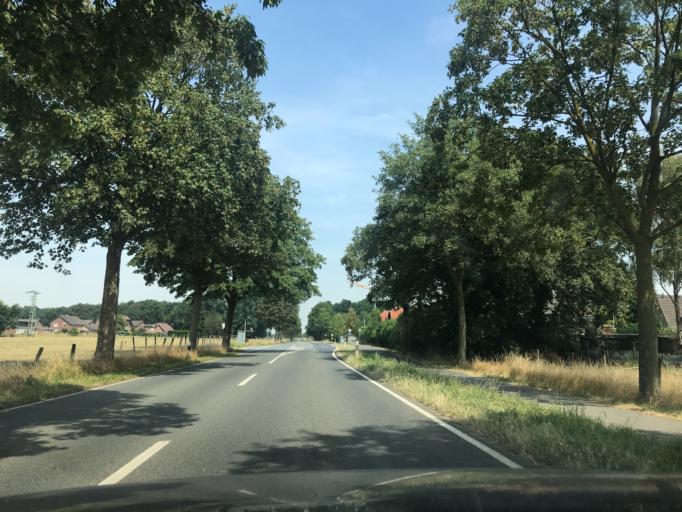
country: DE
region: North Rhine-Westphalia
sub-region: Regierungsbezirk Dusseldorf
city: Issum
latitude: 51.4966
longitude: 6.4182
